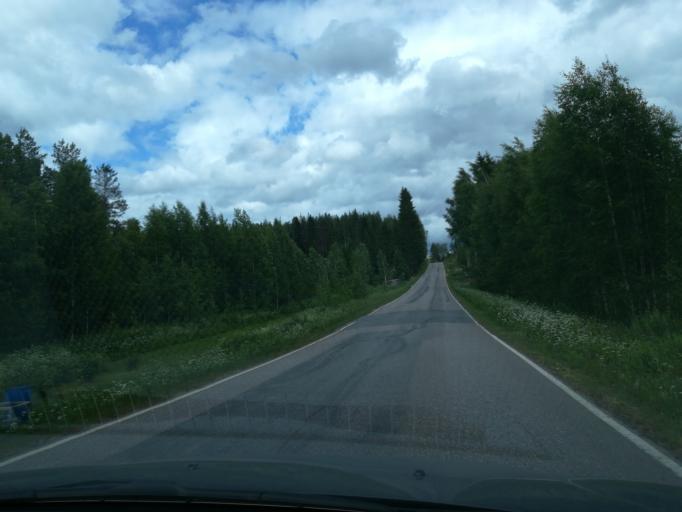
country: FI
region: South Karelia
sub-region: Lappeenranta
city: Savitaipale
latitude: 61.2213
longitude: 27.6996
